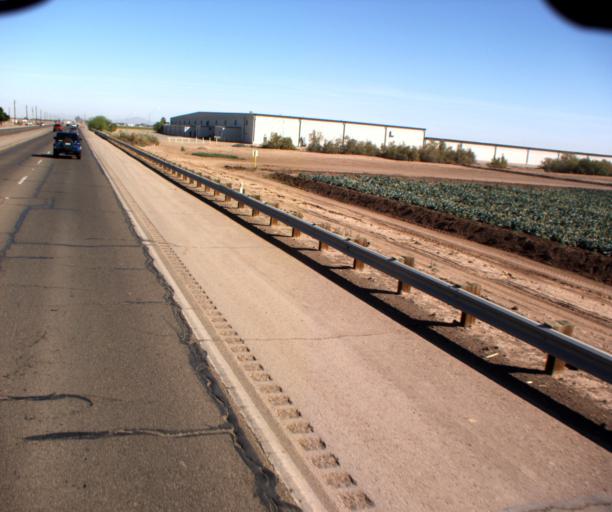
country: US
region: Arizona
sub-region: Yuma County
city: San Luis
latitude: 32.5265
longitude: -114.7866
